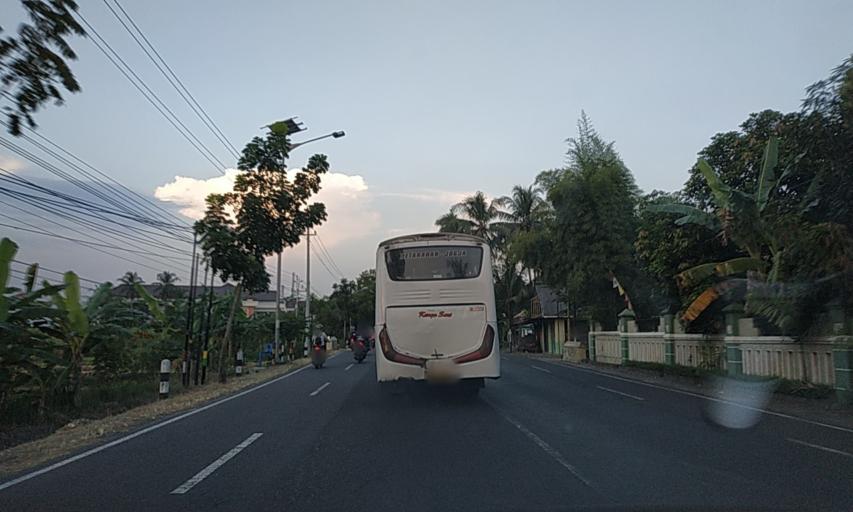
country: ID
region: Daerah Istimewa Yogyakarta
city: Srandakan
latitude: -7.8700
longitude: 110.1443
